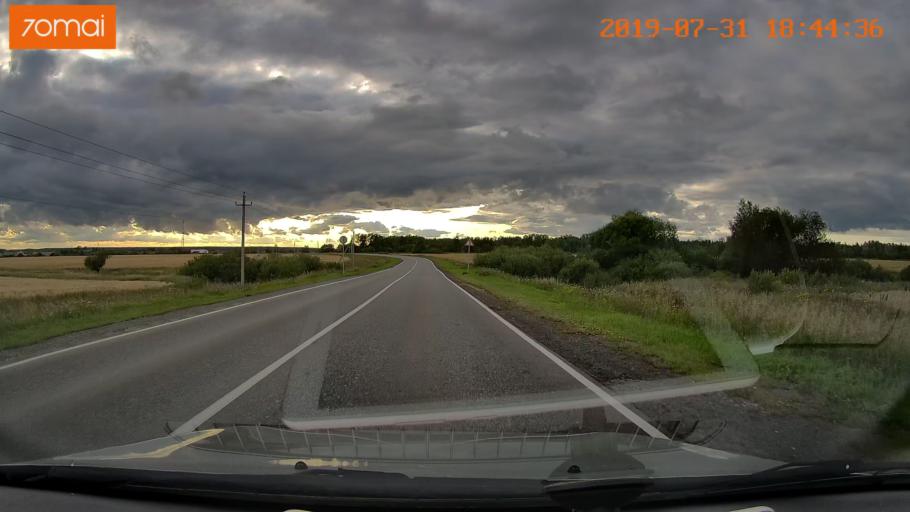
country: RU
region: Moskovskaya
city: Troitskoye
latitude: 55.2510
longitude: 38.5483
